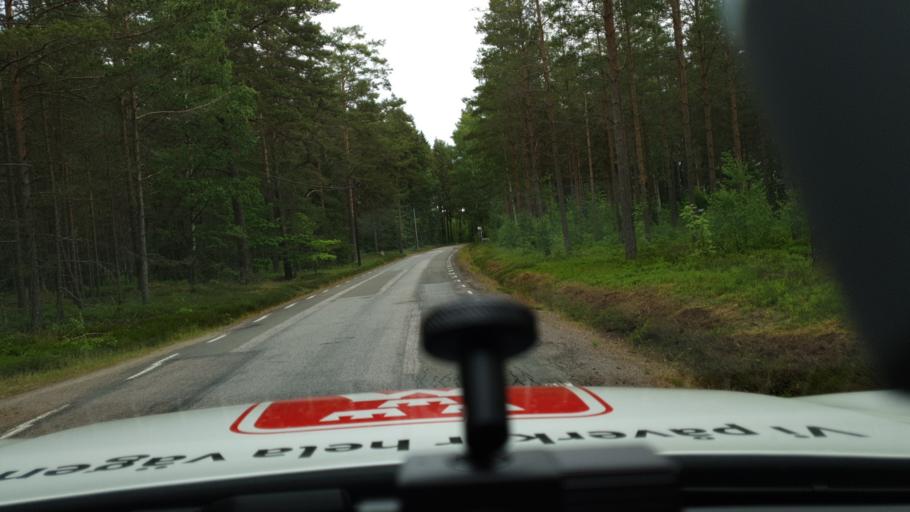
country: SE
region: Vaestra Goetaland
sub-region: Karlsborgs Kommun
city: Molltorp
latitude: 58.4292
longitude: 14.3768
